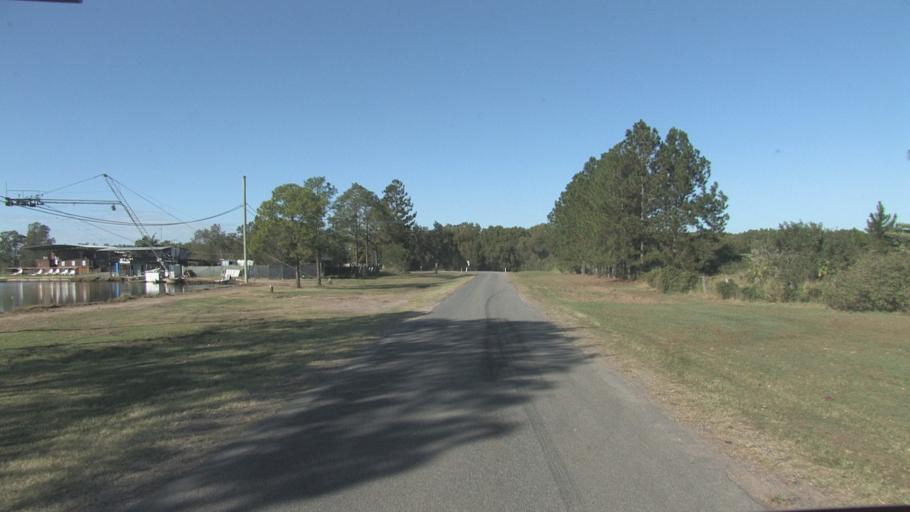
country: AU
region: Queensland
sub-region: Gold Coast
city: Yatala
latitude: -27.6903
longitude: 153.2606
